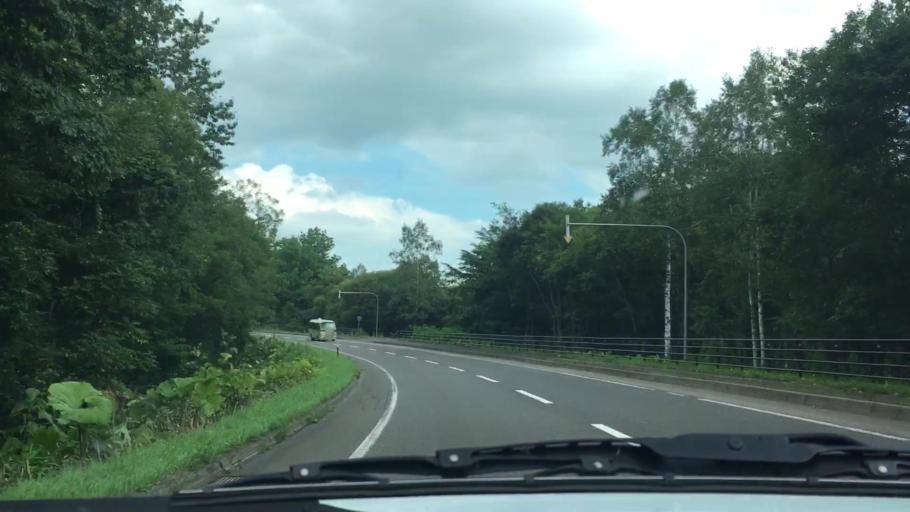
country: JP
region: Hokkaido
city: Otofuke
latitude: 43.3459
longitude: 143.2732
